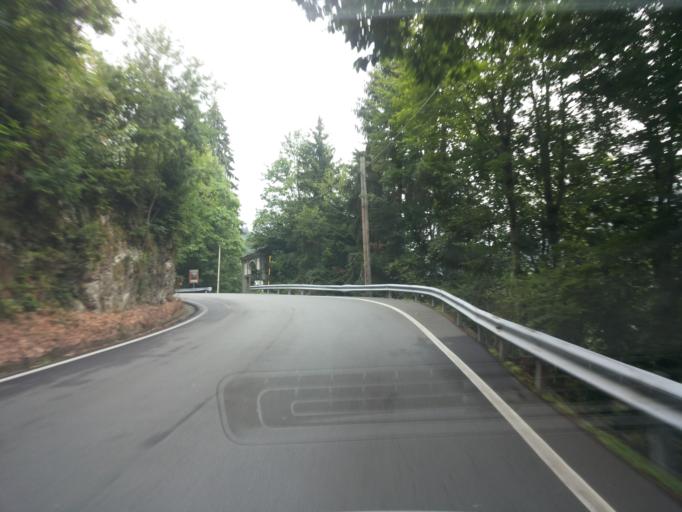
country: IT
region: Piedmont
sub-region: Provincia di Biella
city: Pollone
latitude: 45.6158
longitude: 7.9861
